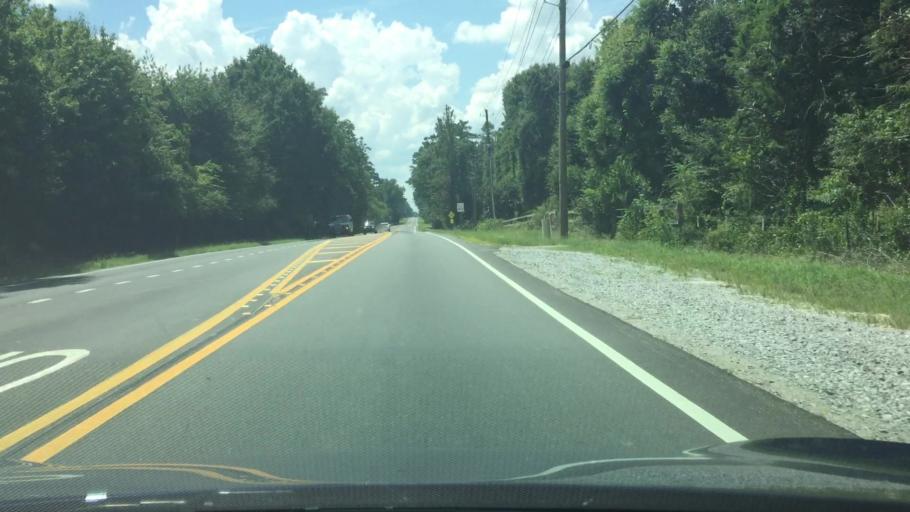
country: US
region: Alabama
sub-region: Montgomery County
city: Pike Road
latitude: 32.3464
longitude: -86.0950
